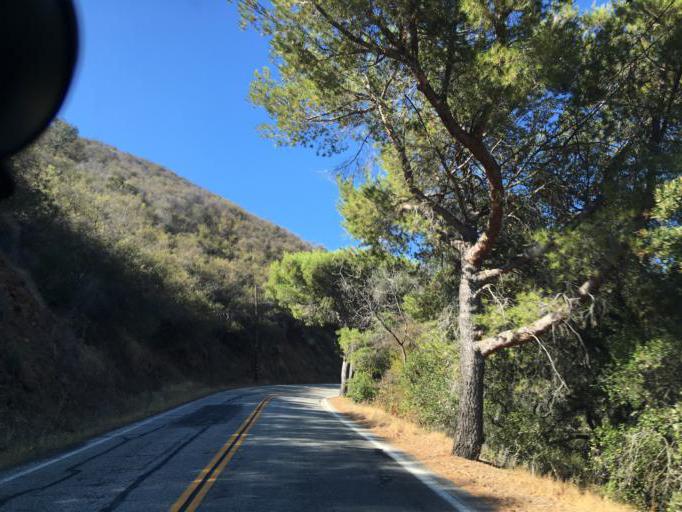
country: US
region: California
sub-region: Ventura County
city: Casa Conejo
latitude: 34.0770
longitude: -118.9231
